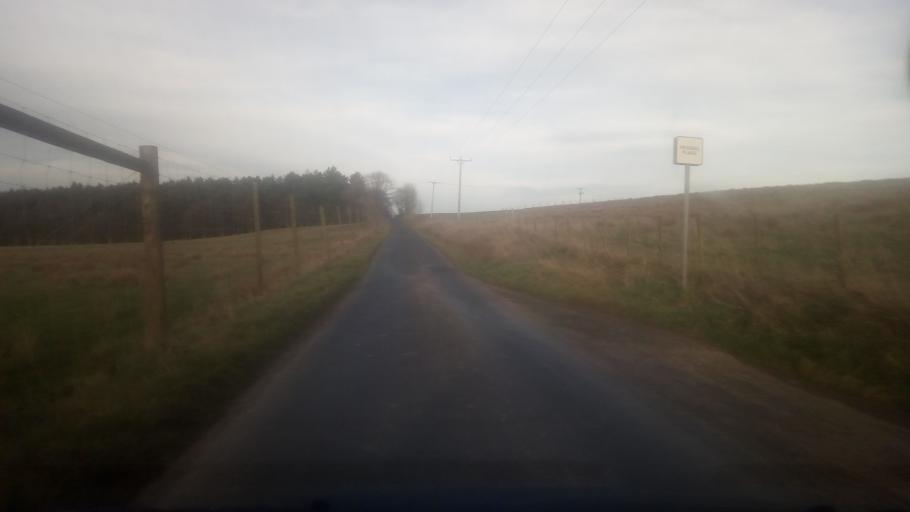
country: GB
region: Scotland
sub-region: The Scottish Borders
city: Jedburgh
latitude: 55.4077
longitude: -2.5226
